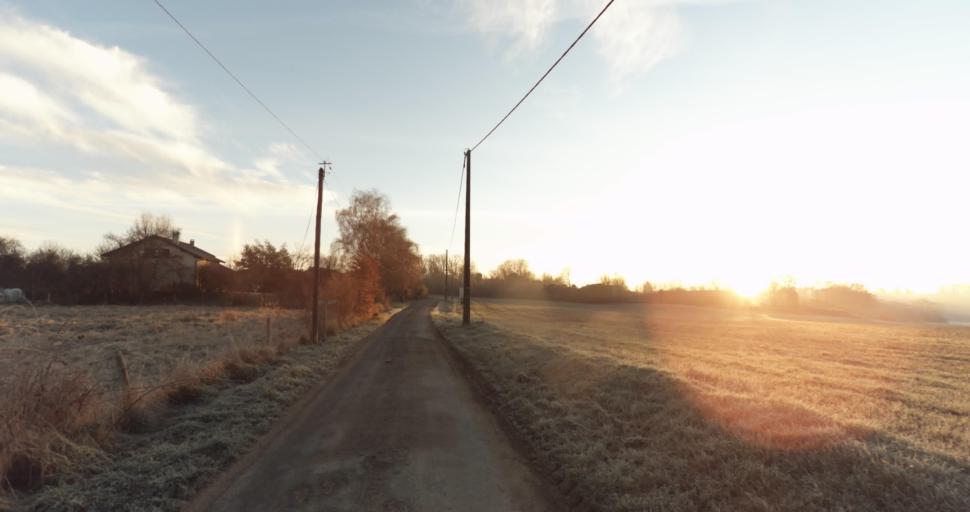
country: FR
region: Limousin
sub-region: Departement de la Haute-Vienne
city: Aixe-sur-Vienne
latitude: 45.8136
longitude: 1.1297
